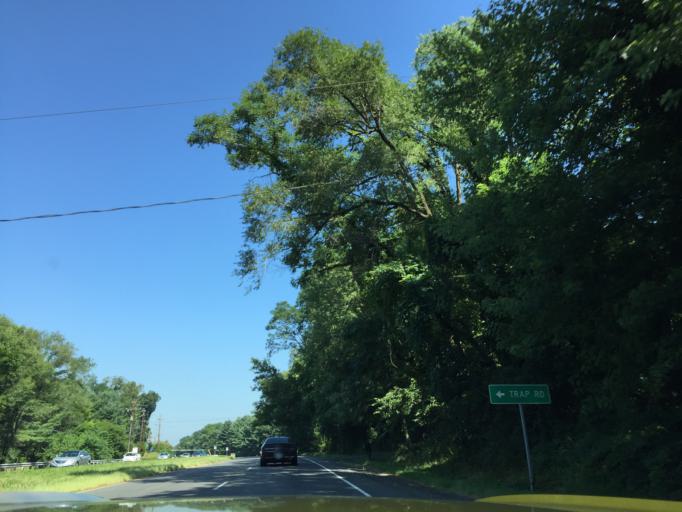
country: US
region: Virginia
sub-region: Fairfax County
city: Wolf Trap
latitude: 38.9488
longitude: -77.2608
